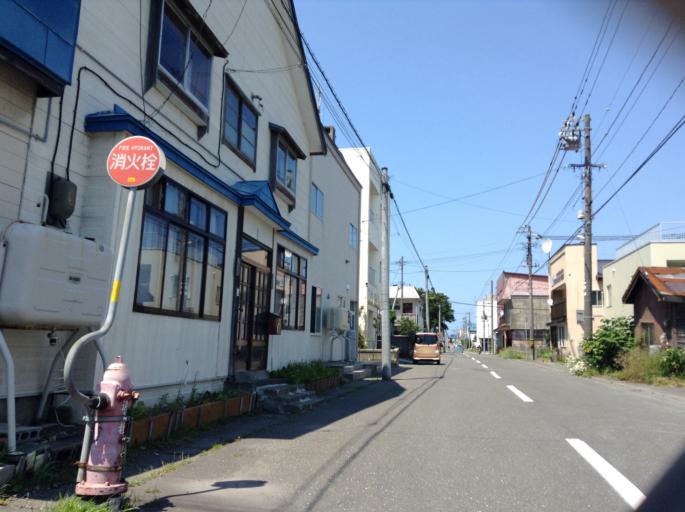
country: JP
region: Hokkaido
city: Wakkanai
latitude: 45.4180
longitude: 141.6730
